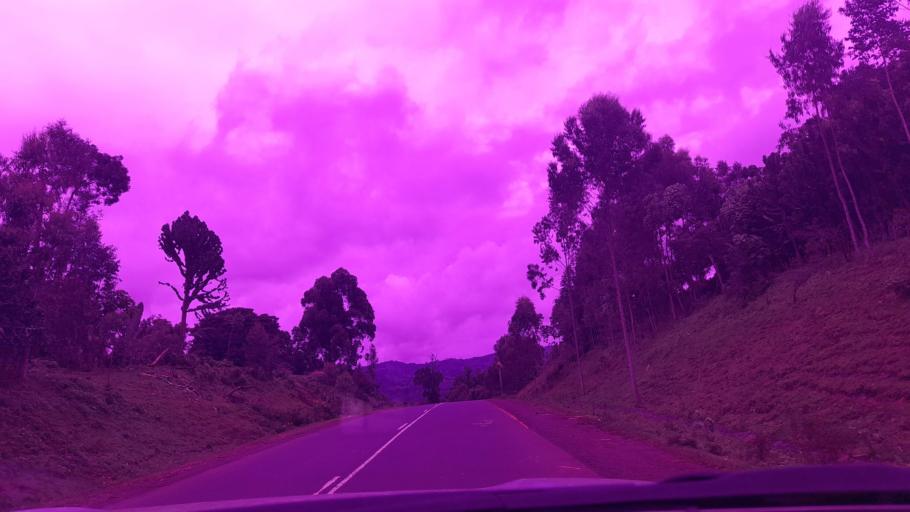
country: ET
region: Southern Nations, Nationalities, and People's Region
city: Bonga
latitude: 7.2881
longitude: 35.9753
